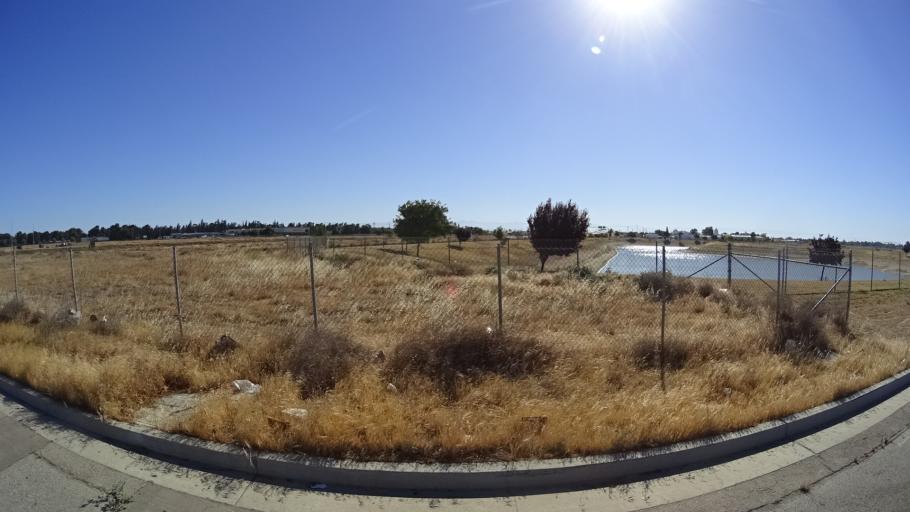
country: US
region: California
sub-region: Fresno County
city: West Park
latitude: 36.7371
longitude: -119.8306
